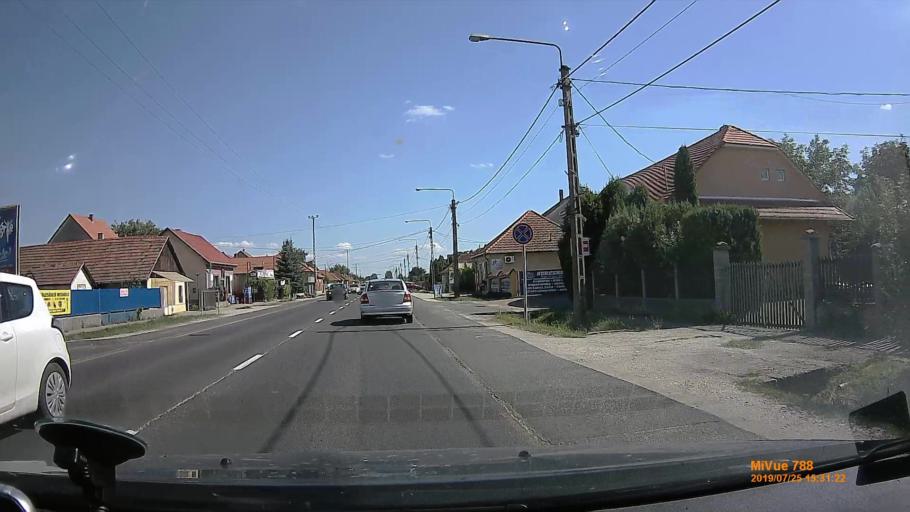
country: HU
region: Borsod-Abauj-Zemplen
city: Malyi
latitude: 48.0139
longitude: 20.8239
